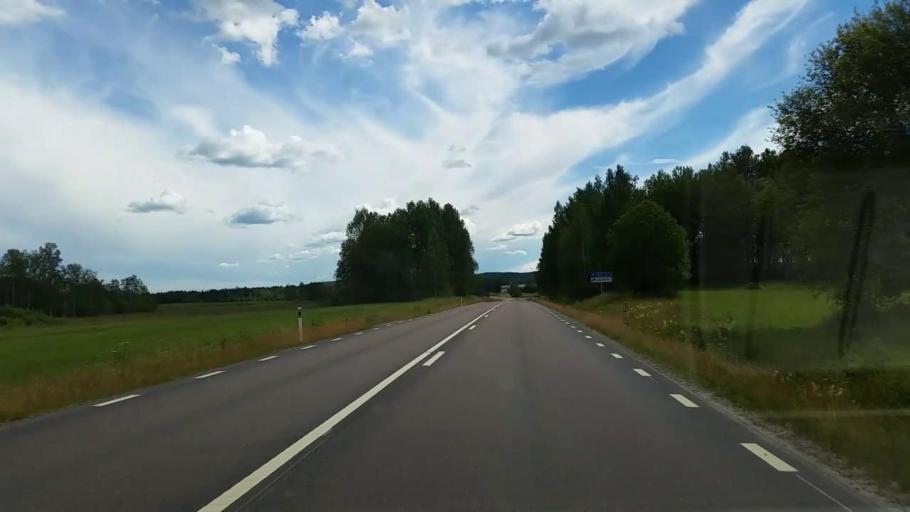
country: SE
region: Gaevleborg
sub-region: Ovanakers Kommun
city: Edsbyn
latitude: 61.3801
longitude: 15.8351
